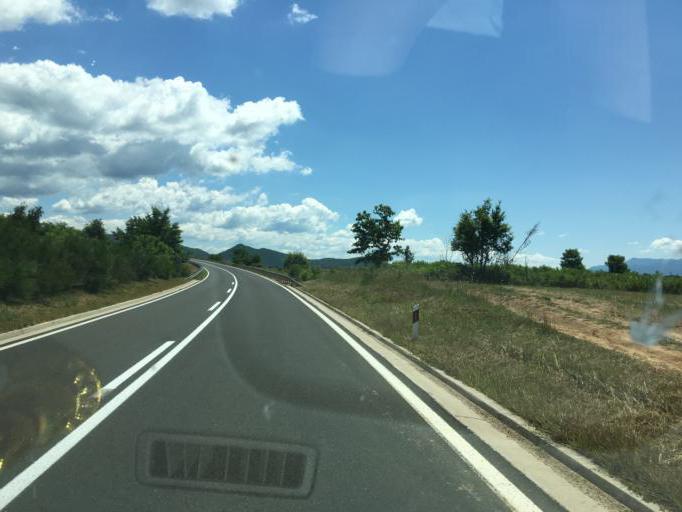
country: HR
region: Licko-Senjska
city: Gospic
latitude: 44.5756
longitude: 15.4063
